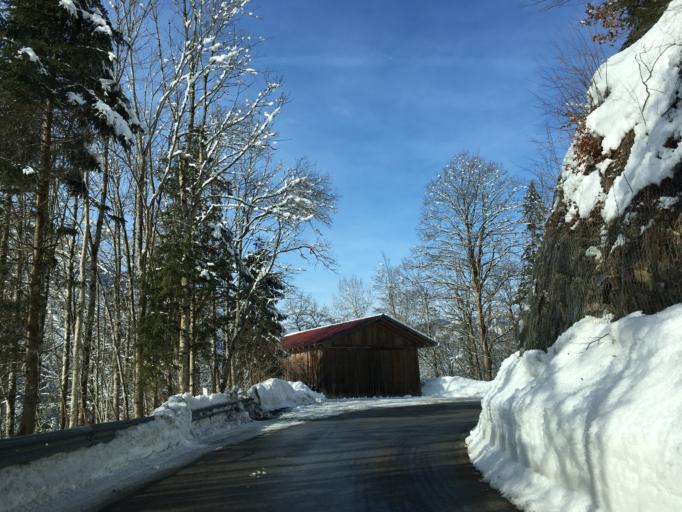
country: DE
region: Bavaria
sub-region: Upper Bavaria
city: Burg Unter-Falkenstein
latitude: 47.6580
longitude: 12.1207
